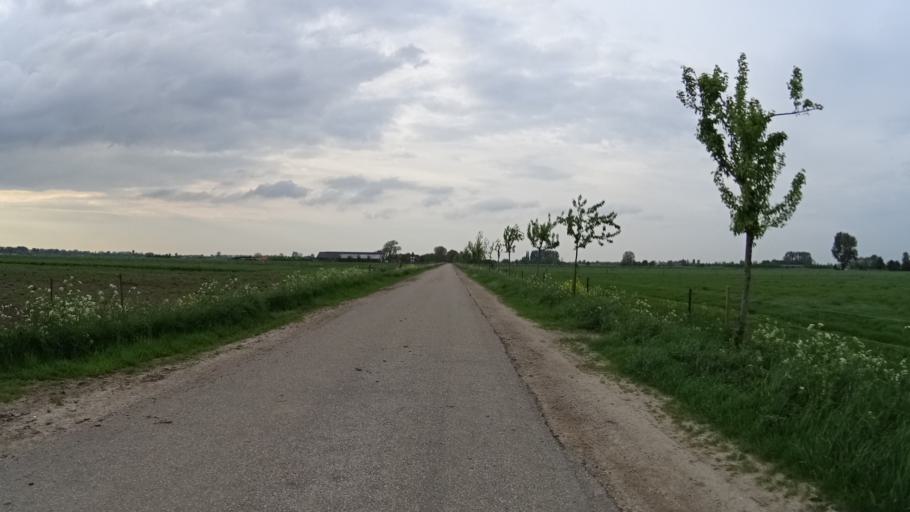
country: NL
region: North Brabant
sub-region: Gemeente Aalburg
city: Aalburg
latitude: 51.7498
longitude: 5.1024
